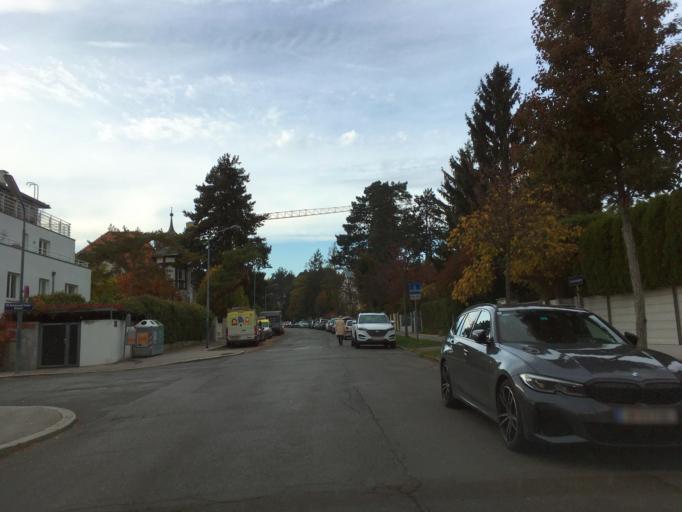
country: AT
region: Lower Austria
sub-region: Politischer Bezirk Korneuburg
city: Langenzersdorf
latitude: 48.2462
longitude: 16.3264
